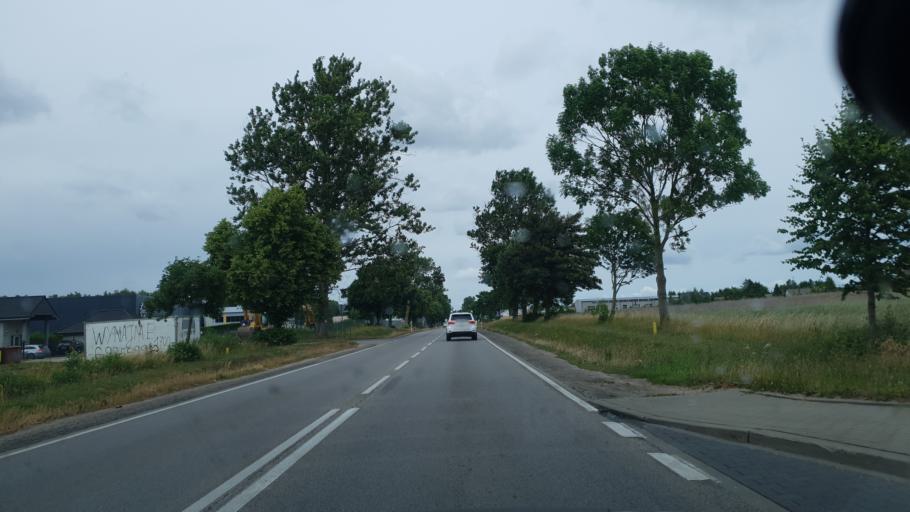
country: PL
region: Pomeranian Voivodeship
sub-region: Powiat kartuski
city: Banino
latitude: 54.4032
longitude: 18.3624
